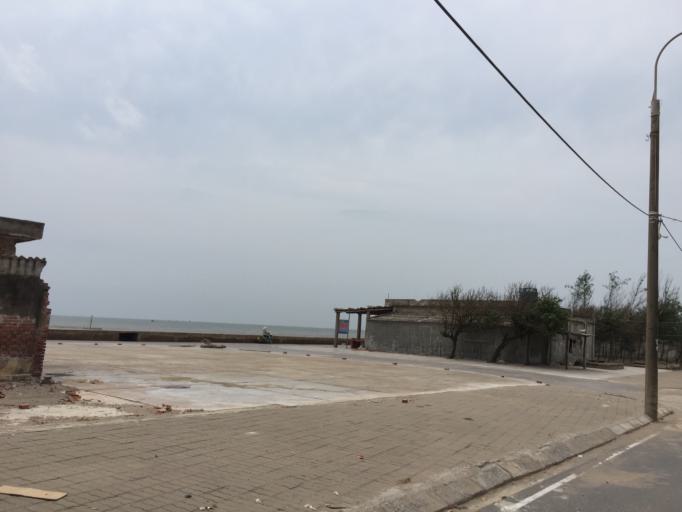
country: VN
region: Ninh Binh
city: Thi Tran Phat Diem
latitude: 20.0343
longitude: 106.2269
